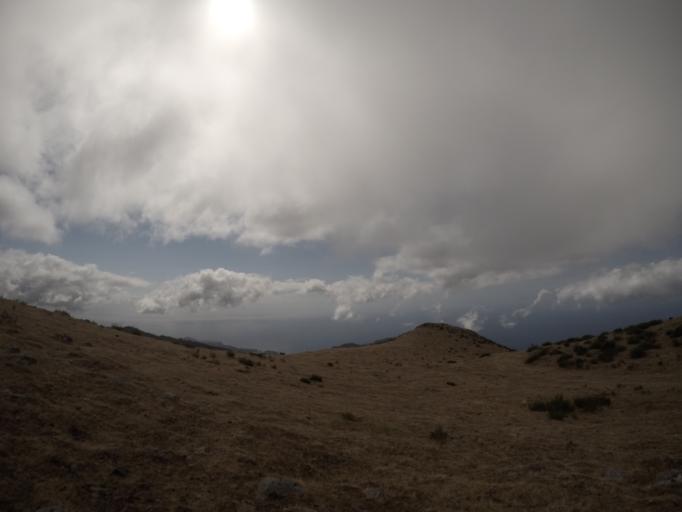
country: PT
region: Madeira
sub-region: Camara de Lobos
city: Curral das Freiras
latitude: 32.7158
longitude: -17.0034
